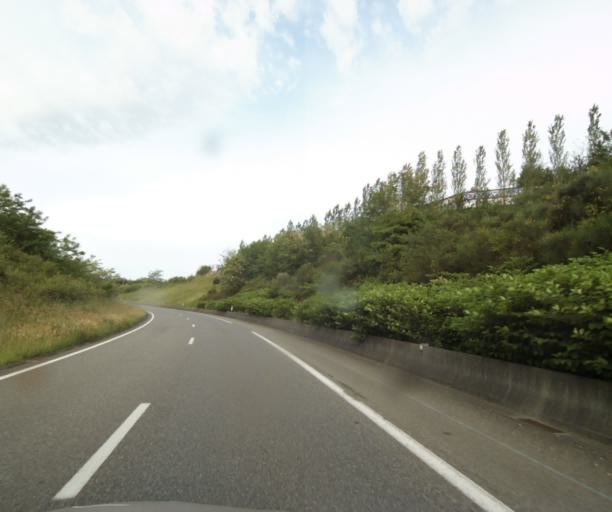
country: FR
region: Aquitaine
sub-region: Departement des Pyrenees-Atlantiques
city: Mouguerre
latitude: 43.4780
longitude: -1.4497
